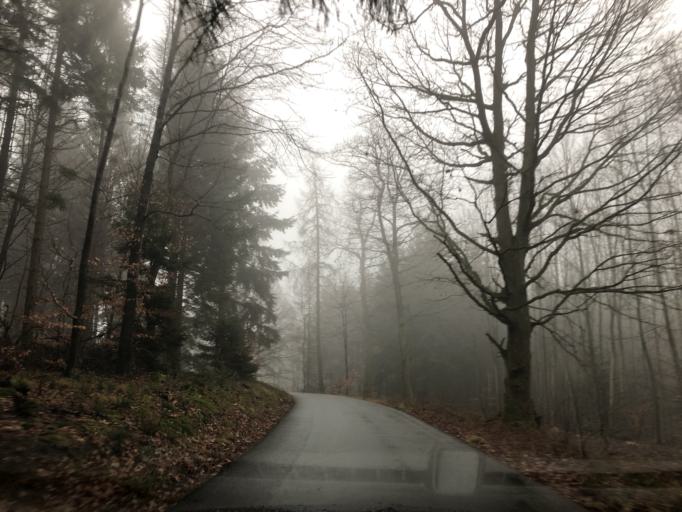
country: DE
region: Baden-Wuerttemberg
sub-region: Karlsruhe Region
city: Wilhelmsfeld
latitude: 49.4500
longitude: 8.7217
